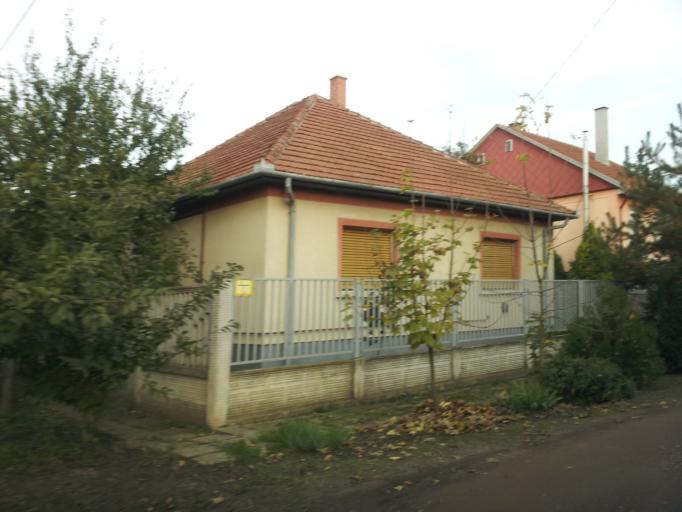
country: HU
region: Pest
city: Nagykata
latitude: 47.4247
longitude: 19.7422
